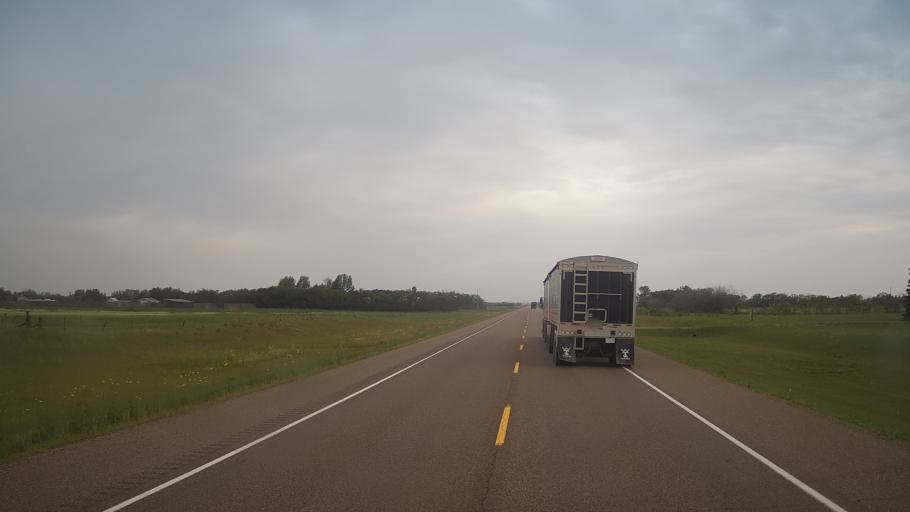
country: CA
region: Saskatchewan
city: Langham
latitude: 52.1294
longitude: -107.0622
